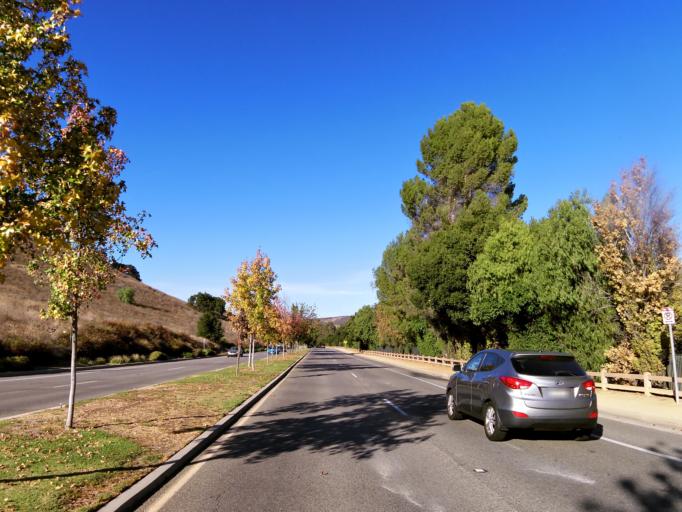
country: US
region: California
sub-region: Ventura County
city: Thousand Oaks
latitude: 34.1855
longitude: -118.8220
